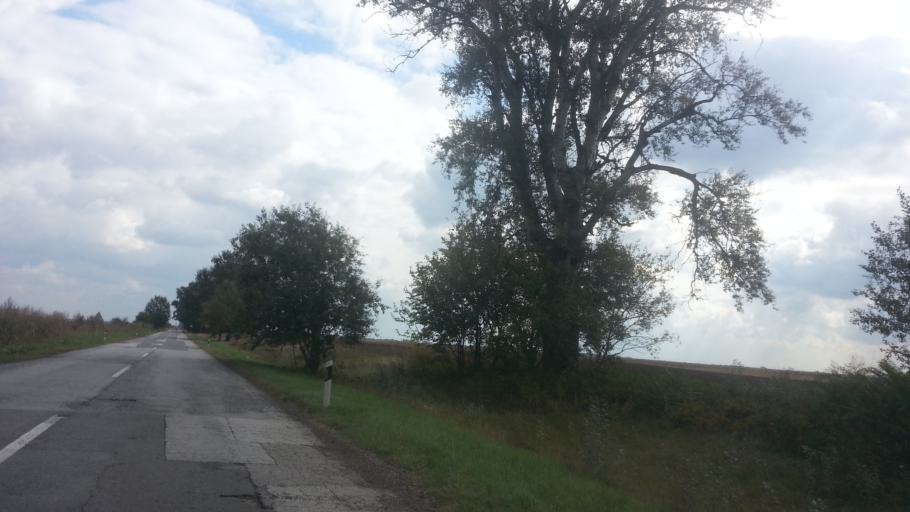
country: RS
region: Autonomna Pokrajina Vojvodina
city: Nova Pazova
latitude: 44.9865
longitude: 20.2348
